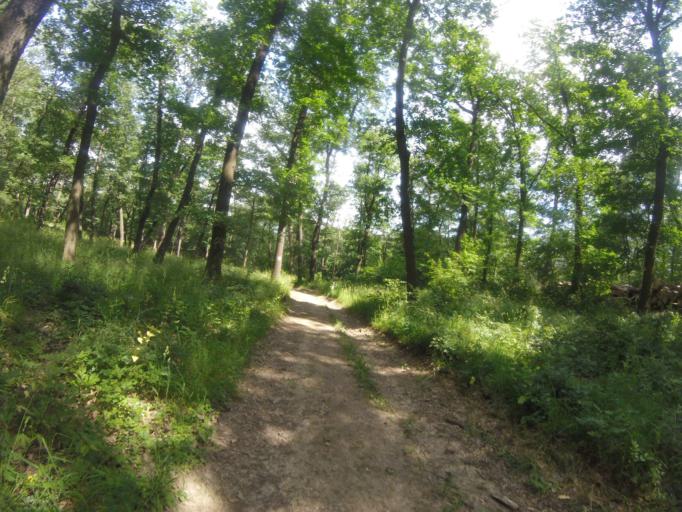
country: HU
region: Fejer
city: Szarliget
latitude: 47.4860
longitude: 18.4740
